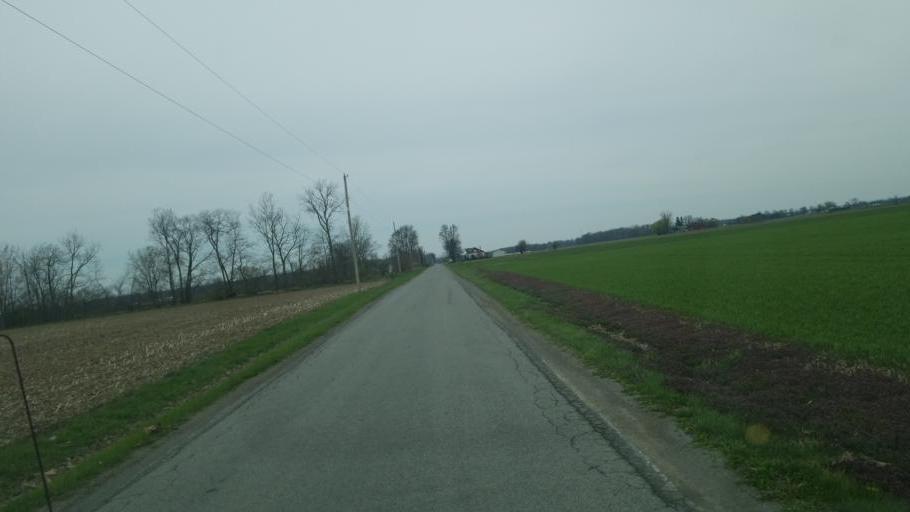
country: US
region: Ohio
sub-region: Wyandot County
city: Carey
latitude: 40.9548
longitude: -83.5132
